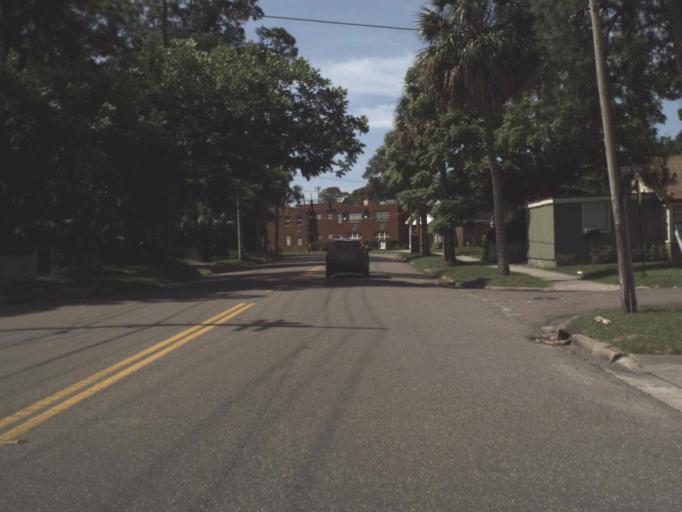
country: US
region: Florida
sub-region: Duval County
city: Jacksonville
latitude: 30.3102
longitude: -81.7053
